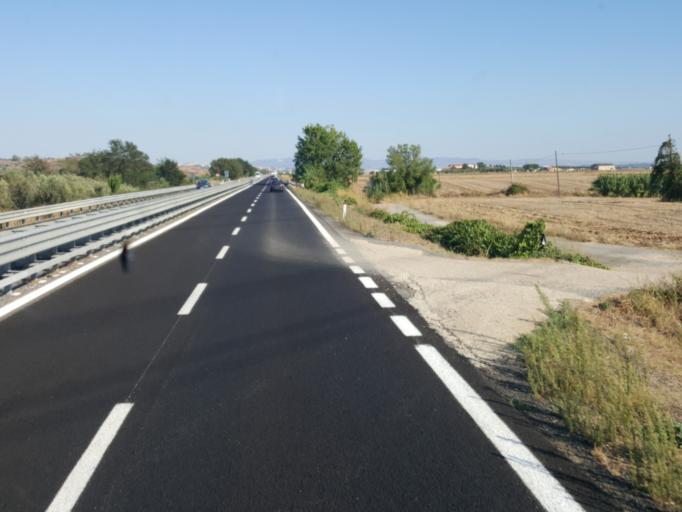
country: IT
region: Latium
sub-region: Provincia di Viterbo
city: Tarquinia
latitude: 42.2790
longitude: 11.6990
